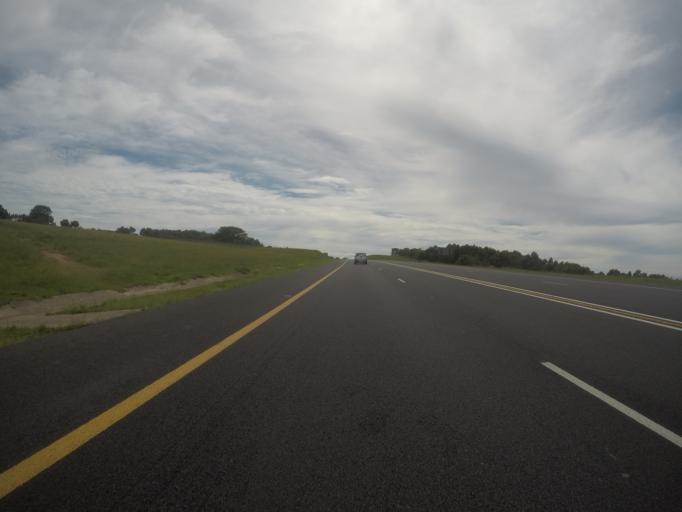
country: ZA
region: KwaZulu-Natal
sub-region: iLembe District Municipality
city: Mandeni
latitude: -29.0903
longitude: 31.6047
